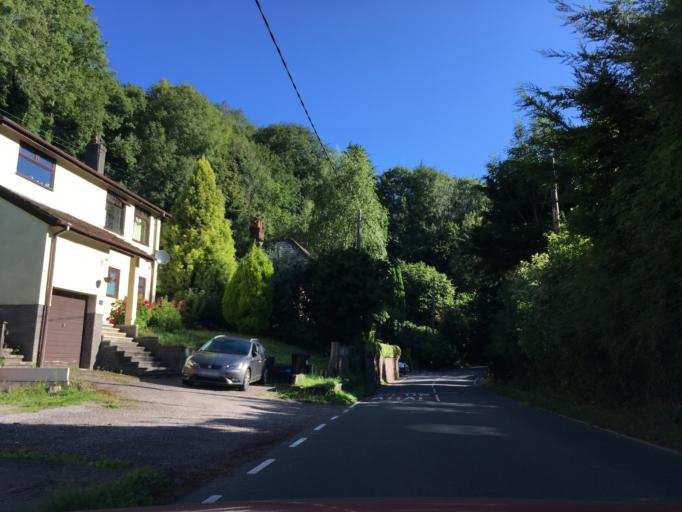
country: GB
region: Wales
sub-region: Monmouthshire
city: Monmouth
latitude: 51.7928
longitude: -2.6730
